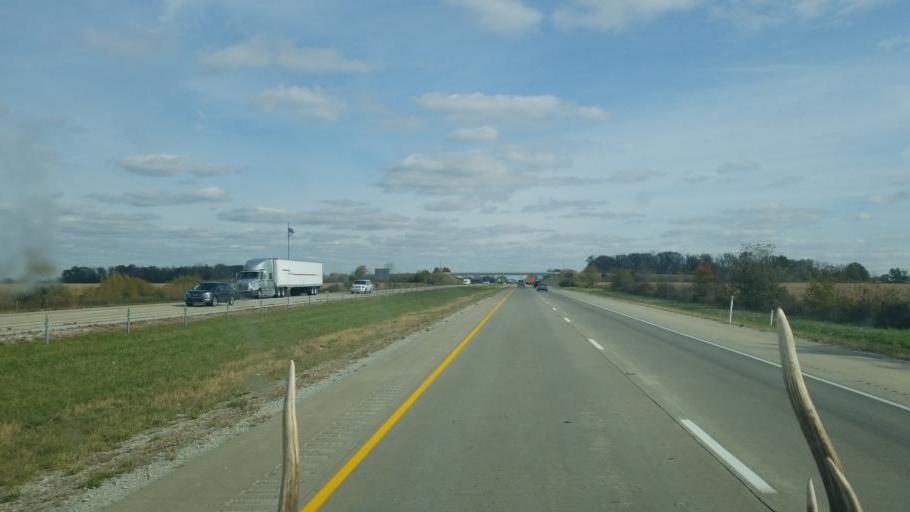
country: US
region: Indiana
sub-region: Marion County
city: Cumberland
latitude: 39.8195
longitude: -85.8831
